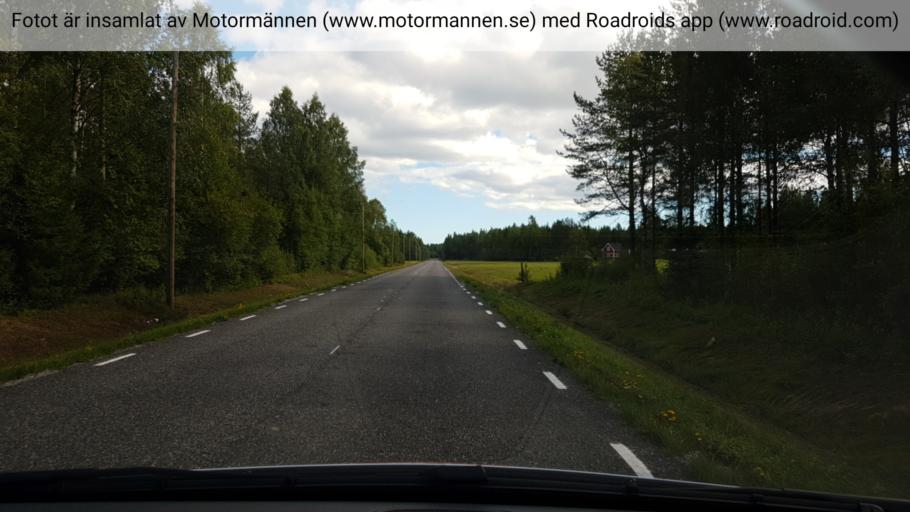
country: SE
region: Vaesterbotten
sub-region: Umea Kommun
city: Hoernefors
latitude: 63.6917
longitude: 19.8529
